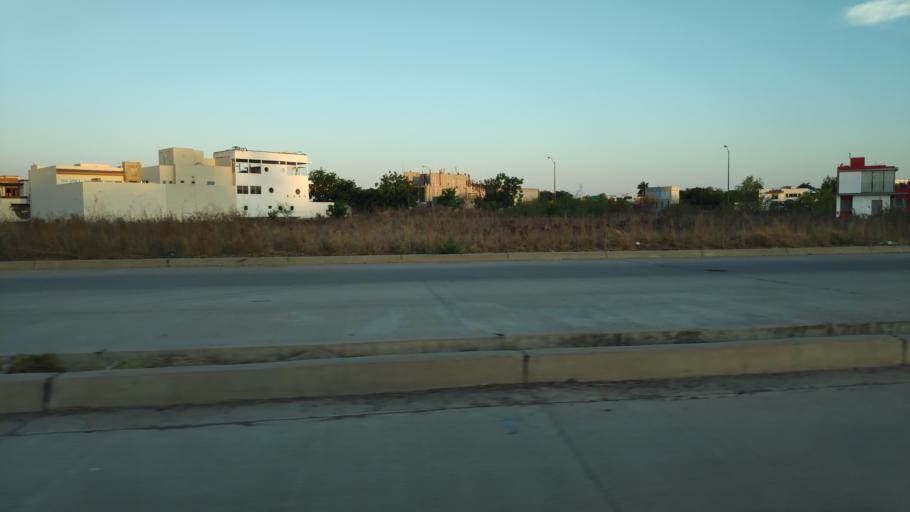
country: MX
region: Sinaloa
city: Culiacan
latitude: 24.8245
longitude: -107.3750
